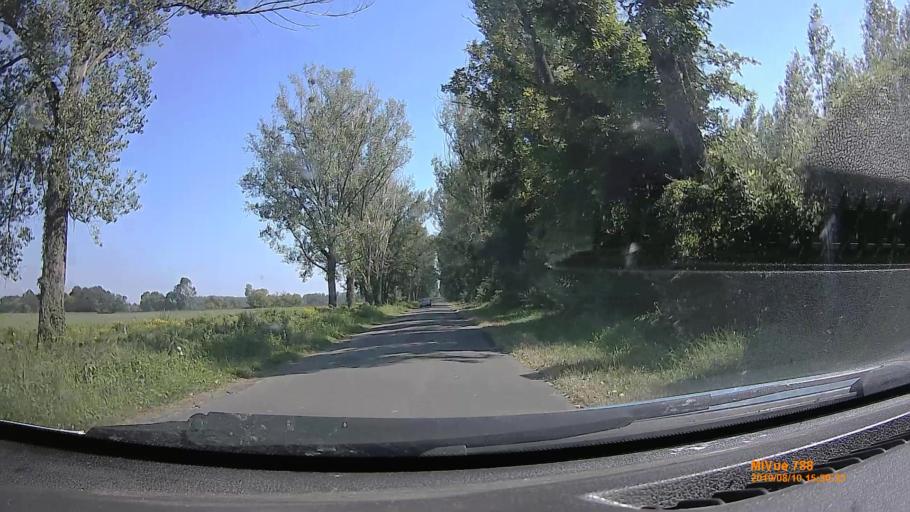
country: HU
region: Somogy
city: Balatonfenyves
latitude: 46.6987
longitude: 17.4870
